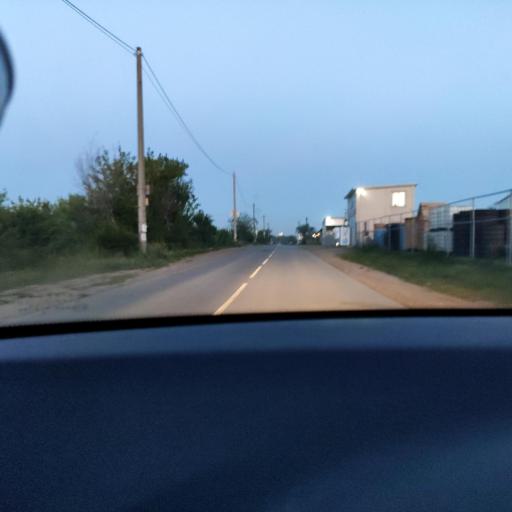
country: RU
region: Samara
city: Novosemeykino
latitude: 53.4025
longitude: 50.3215
